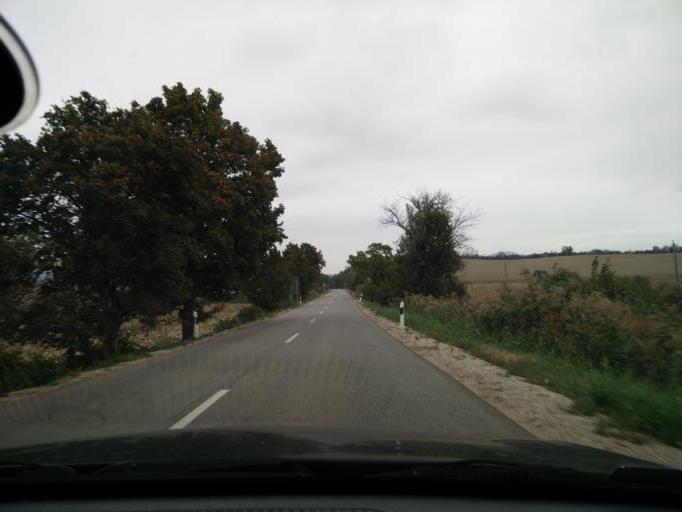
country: HU
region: Komarom-Esztergom
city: Bajna
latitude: 47.6893
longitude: 18.6103
